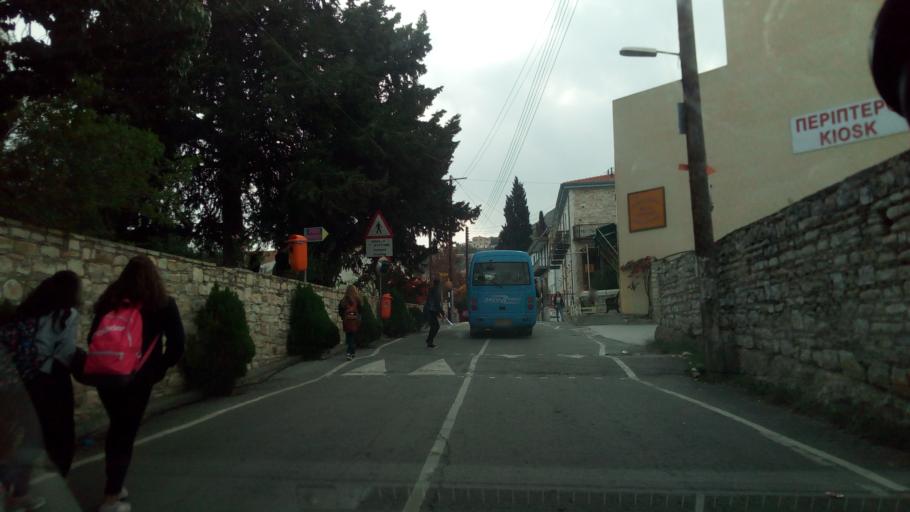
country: CY
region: Lefkosia
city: Lythrodontas
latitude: 34.8686
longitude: 33.3057
